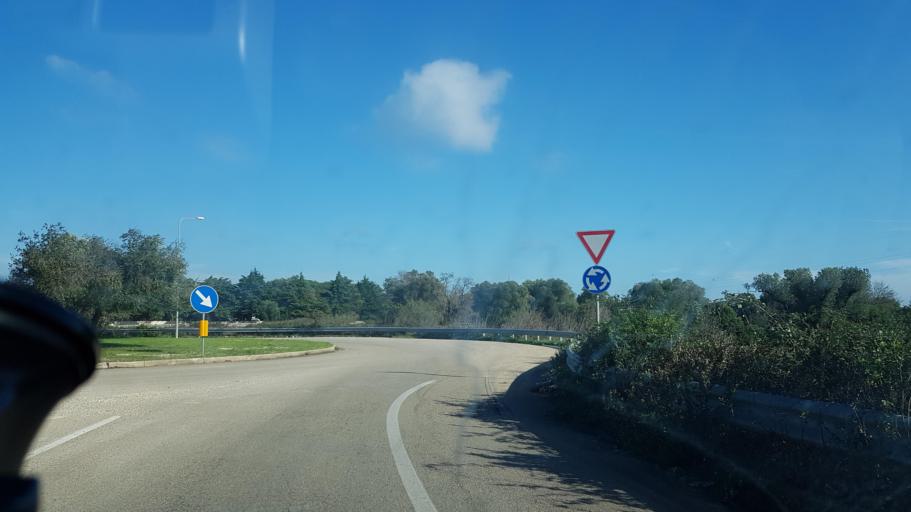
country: IT
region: Apulia
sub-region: Provincia di Brindisi
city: San Vito dei Normanni
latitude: 40.6731
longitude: 17.7097
